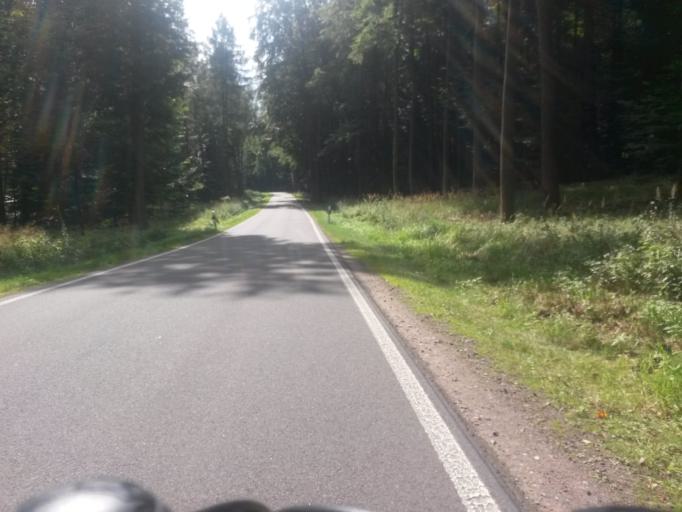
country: DE
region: Brandenburg
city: Angermunde
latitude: 53.0468
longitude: 13.9024
